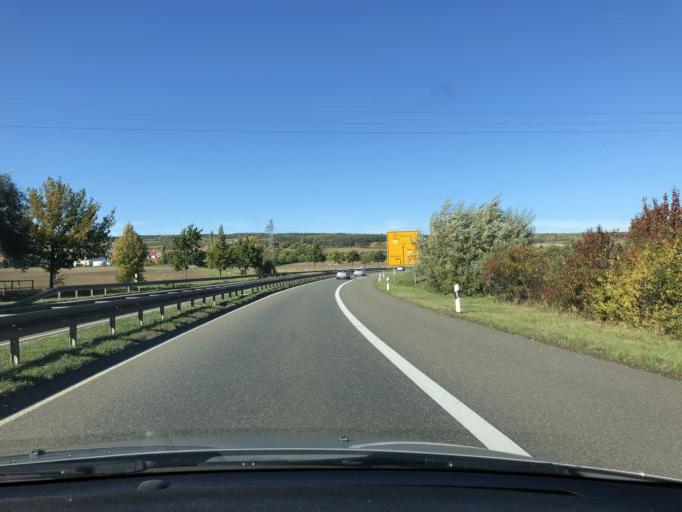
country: DE
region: Thuringia
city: Hopfgarten
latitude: 50.9902
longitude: 11.2889
